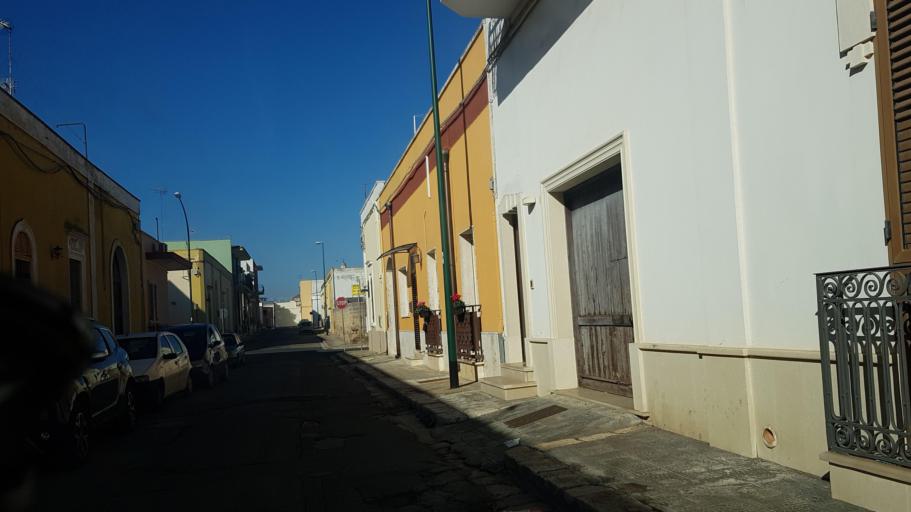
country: IT
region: Apulia
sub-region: Provincia di Lecce
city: Campi Salentina
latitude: 40.3961
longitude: 18.0237
